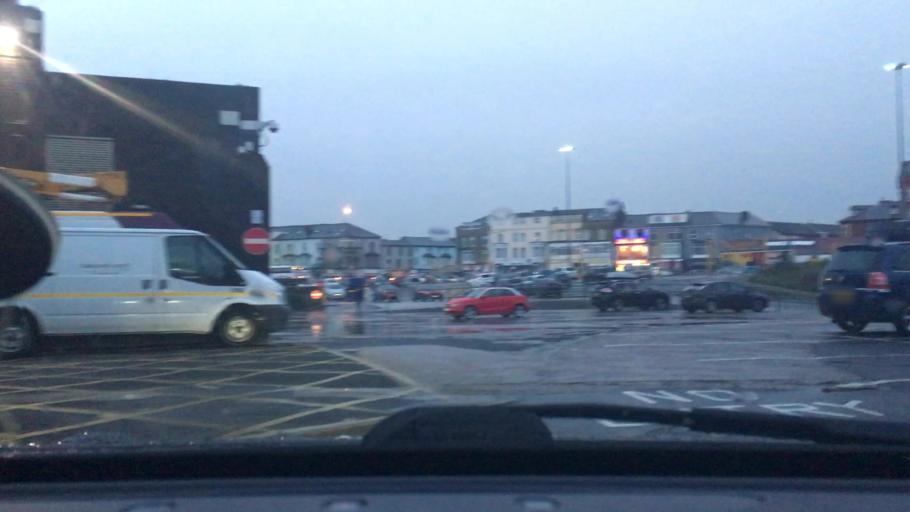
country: GB
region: England
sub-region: Blackpool
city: Blackpool
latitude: 53.8119
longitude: -3.0528
